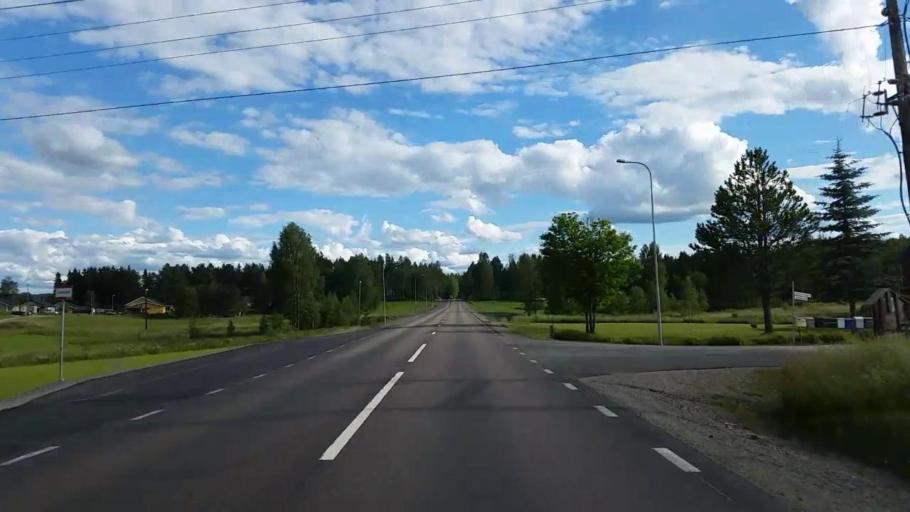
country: SE
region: Gaevleborg
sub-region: Ljusdals Kommun
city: Farila
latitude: 61.9290
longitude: 15.8735
